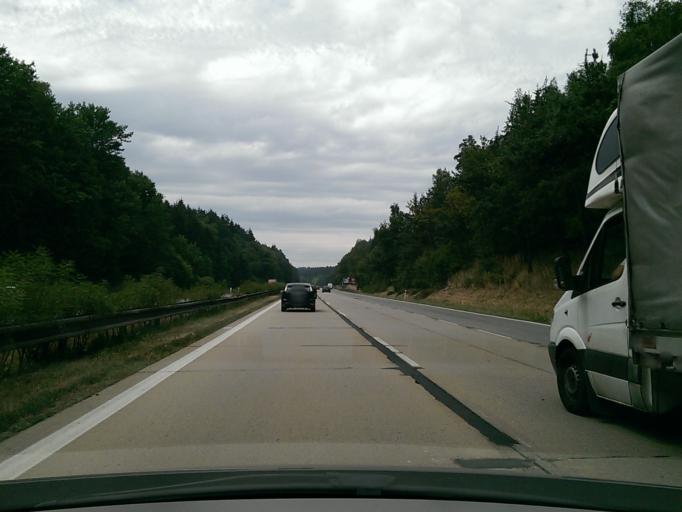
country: CZ
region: Vysocina
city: Kamenice
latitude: 49.4057
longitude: 15.8212
